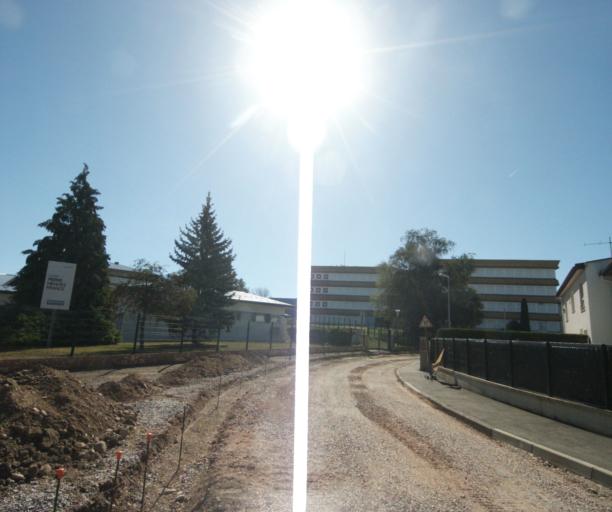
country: FR
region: Lorraine
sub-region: Departement des Vosges
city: Epinal
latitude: 48.1873
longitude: 6.4557
